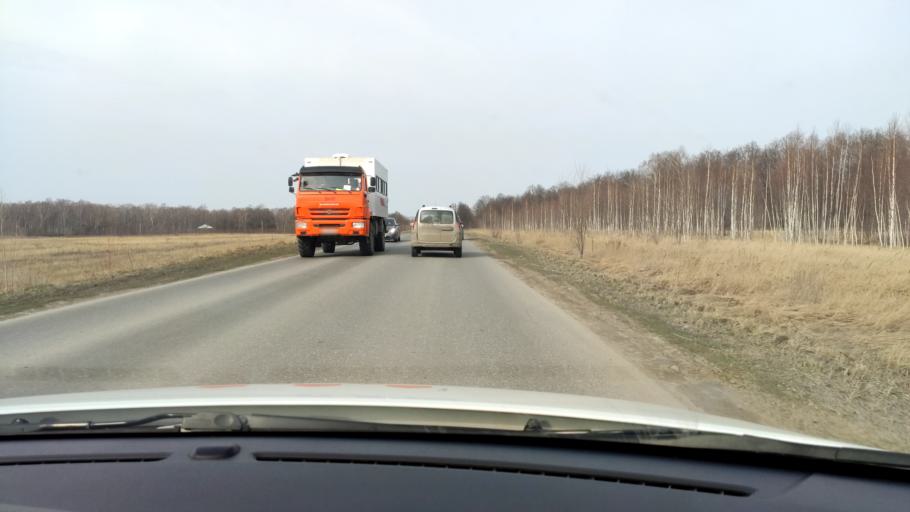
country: RU
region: Tatarstan
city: Stolbishchi
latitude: 55.7149
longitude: 49.1711
